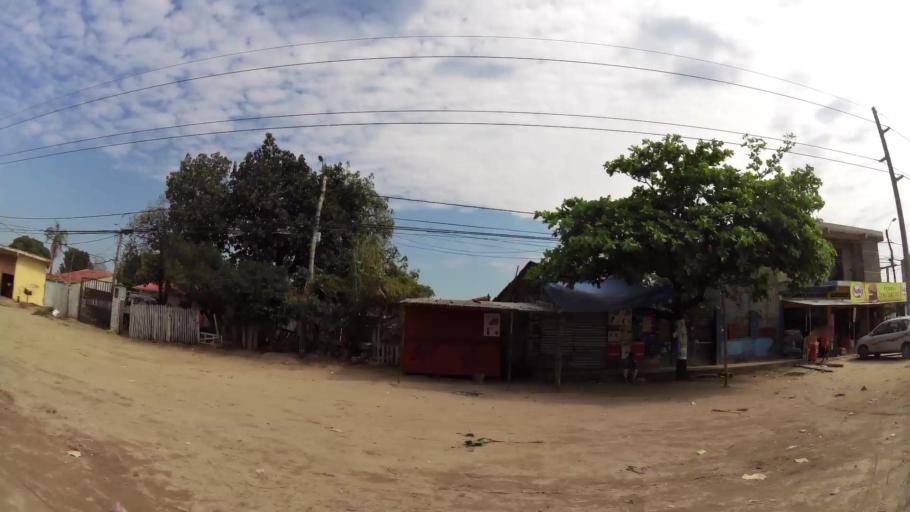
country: BO
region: Santa Cruz
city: Santa Cruz de la Sierra
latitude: -17.7355
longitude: -63.1787
